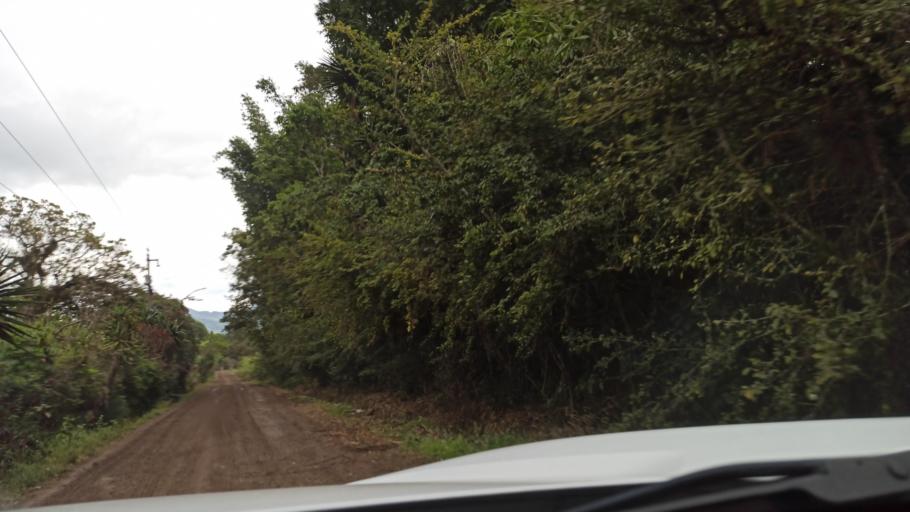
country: MX
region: Veracruz
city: Monte Blanco
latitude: 18.9811
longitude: -97.0115
